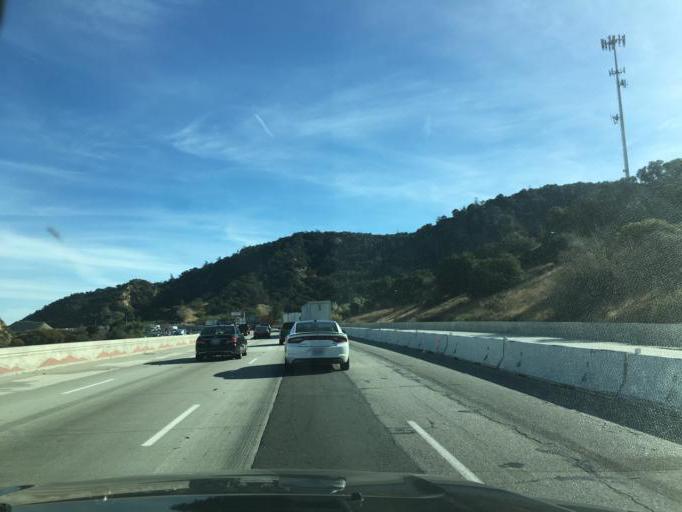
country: US
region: California
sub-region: Los Angeles County
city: Santa Clarita
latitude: 34.3448
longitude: -118.5317
